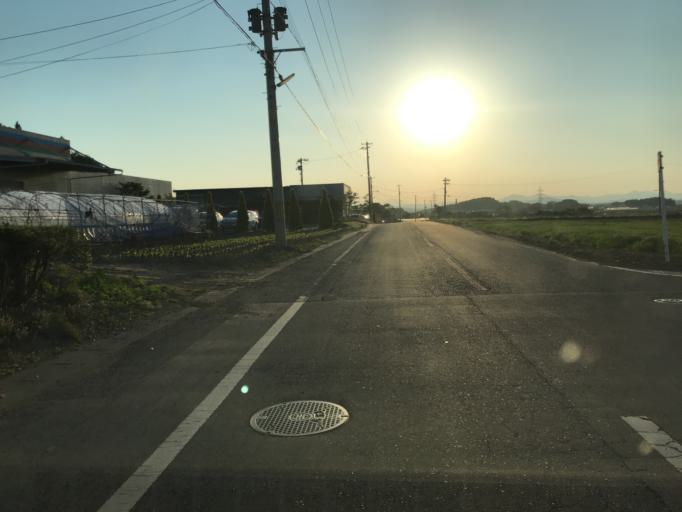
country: JP
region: Fukushima
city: Ishikawa
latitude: 37.1760
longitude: 140.3456
